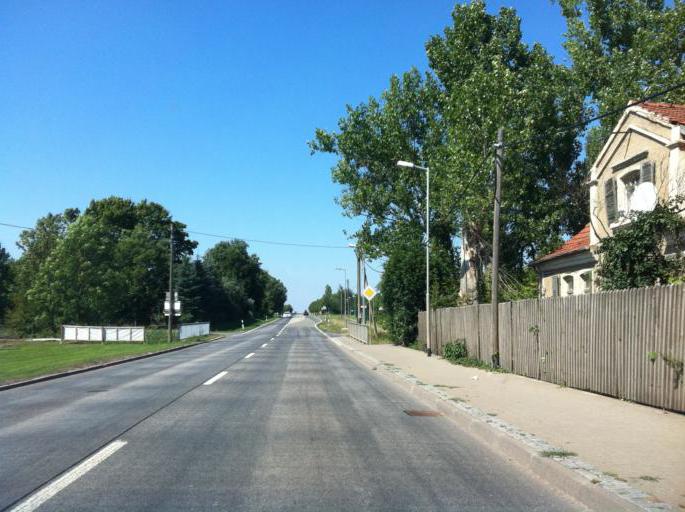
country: DE
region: Thuringia
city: Ballstadt
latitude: 51.0926
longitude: 10.7237
